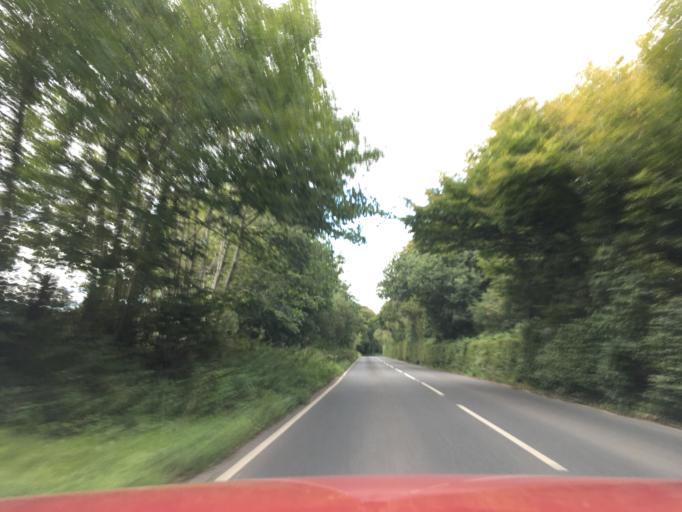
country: GB
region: England
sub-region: Devon
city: Honiton
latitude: 50.7494
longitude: -3.2084
